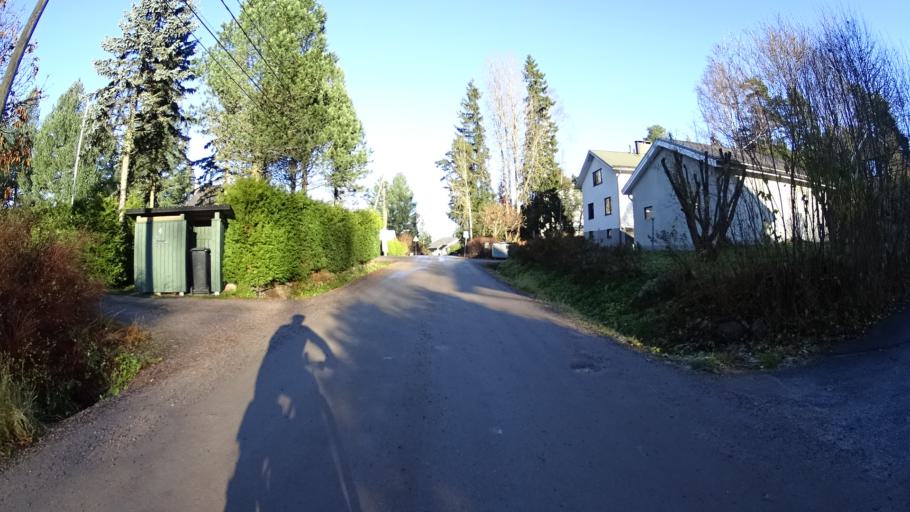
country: FI
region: Uusimaa
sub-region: Helsinki
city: Teekkarikylae
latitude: 60.2299
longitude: 24.8328
